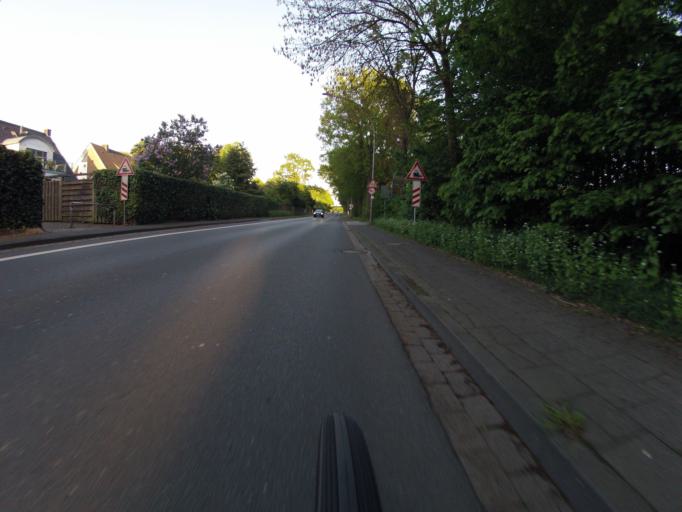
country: DE
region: North Rhine-Westphalia
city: Ibbenburen
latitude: 52.2675
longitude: 7.7311
